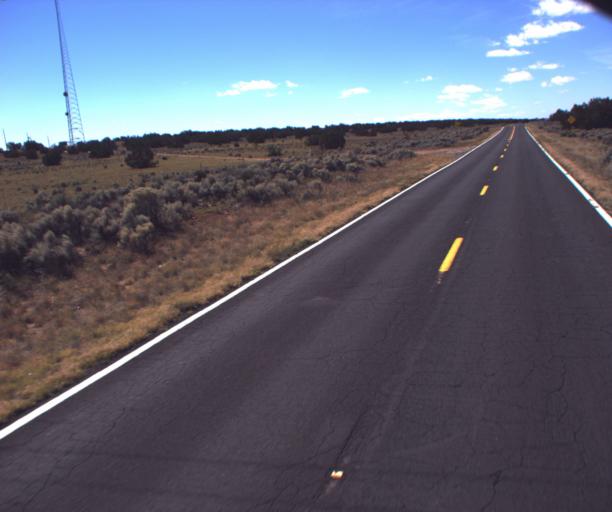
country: US
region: Arizona
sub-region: Apache County
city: Houck
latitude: 34.9108
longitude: -109.2239
